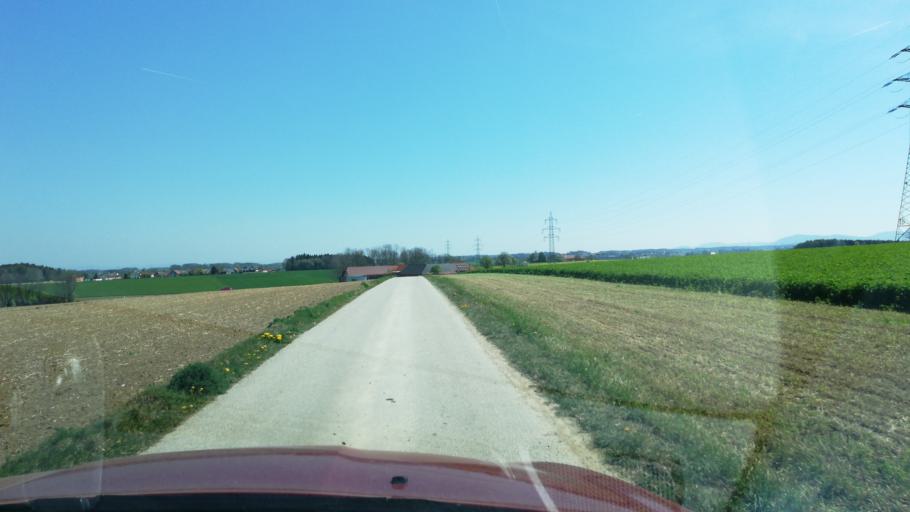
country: AT
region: Upper Austria
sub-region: Politischer Bezirk Steyr-Land
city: Pfarrkirchen bei Bad Hall
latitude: 48.0446
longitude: 14.1801
